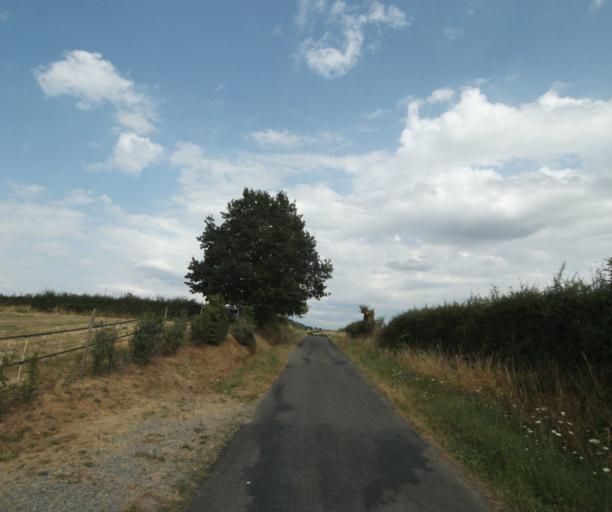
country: FR
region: Bourgogne
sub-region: Departement de Saone-et-Loire
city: Gueugnon
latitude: 46.5998
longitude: 4.0879
